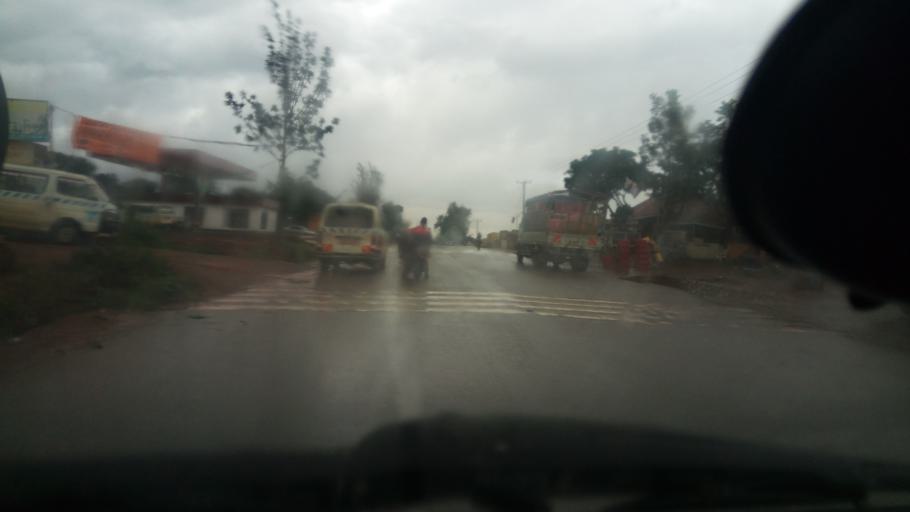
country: UG
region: Central Region
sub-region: Wakiso District
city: Wakiso
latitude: 0.4119
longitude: 32.4604
